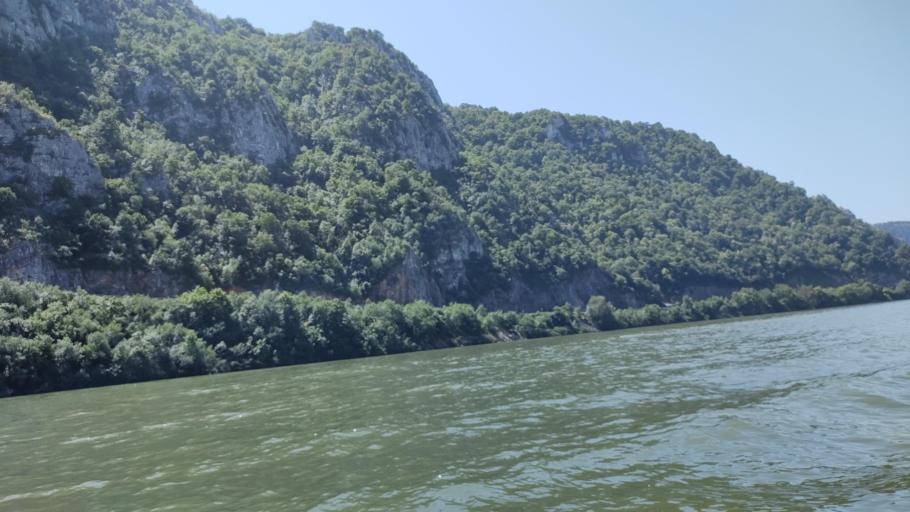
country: RO
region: Mehedinti
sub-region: Comuna Dubova
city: Dubova
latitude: 44.6319
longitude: 22.2875
